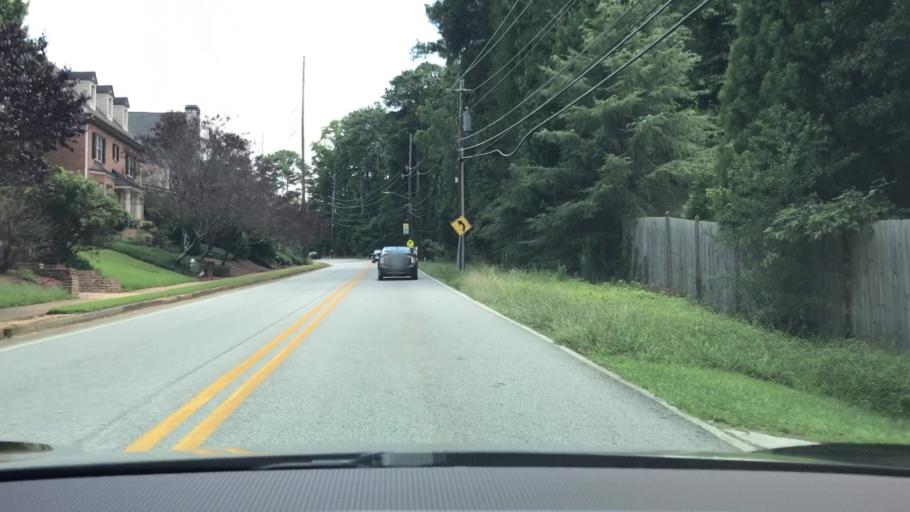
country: US
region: Georgia
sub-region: DeKalb County
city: Tucker
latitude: 33.8527
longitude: -84.2624
